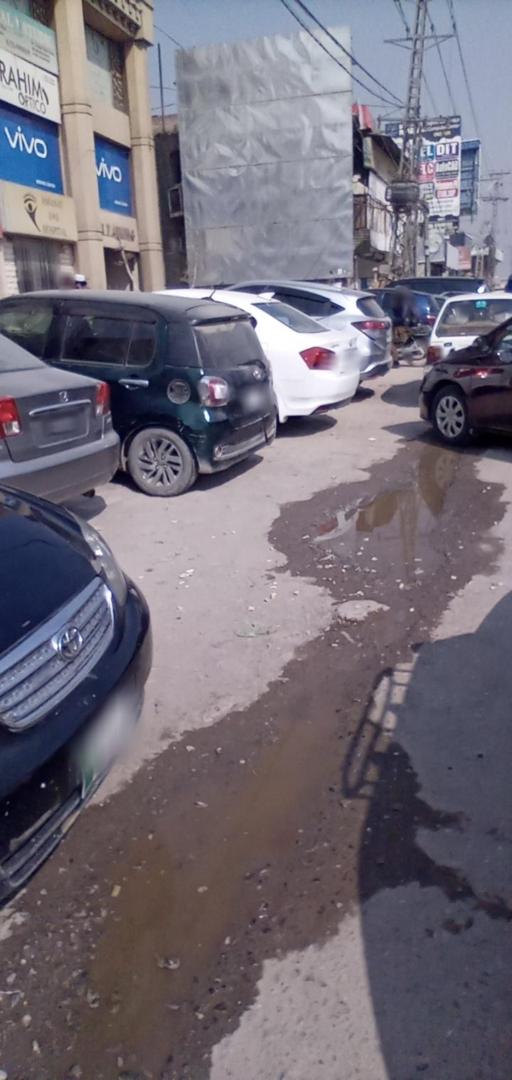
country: PK
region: Khyber Pakhtunkhwa
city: Peshawar
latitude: 34.0083
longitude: 71.5112
